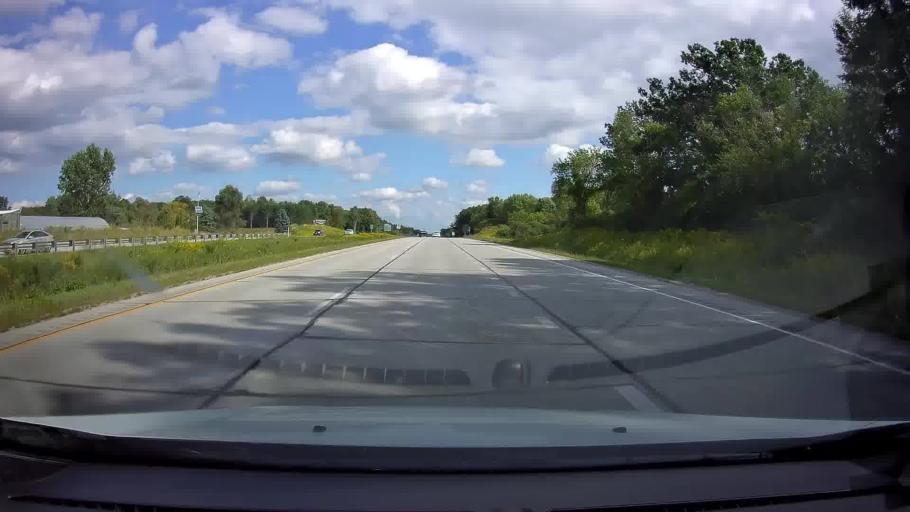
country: US
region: Wisconsin
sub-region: Brown County
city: Howard
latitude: 44.5572
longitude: -88.1230
